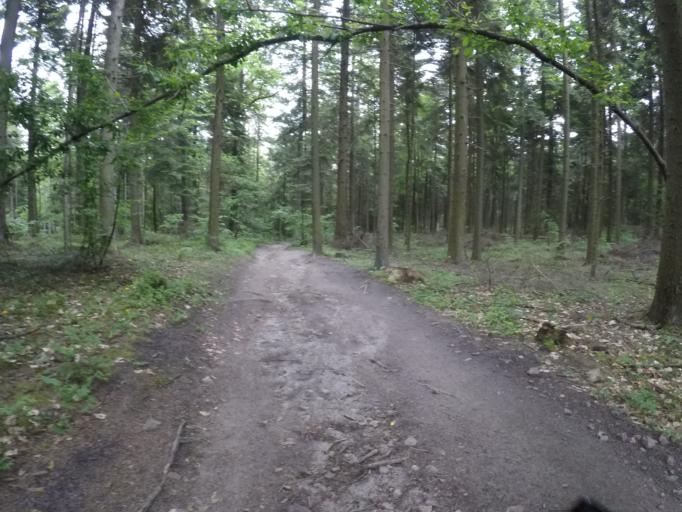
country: PL
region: Swietokrzyskie
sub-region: Powiat kielecki
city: Kielce
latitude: 50.8362
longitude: 20.6011
